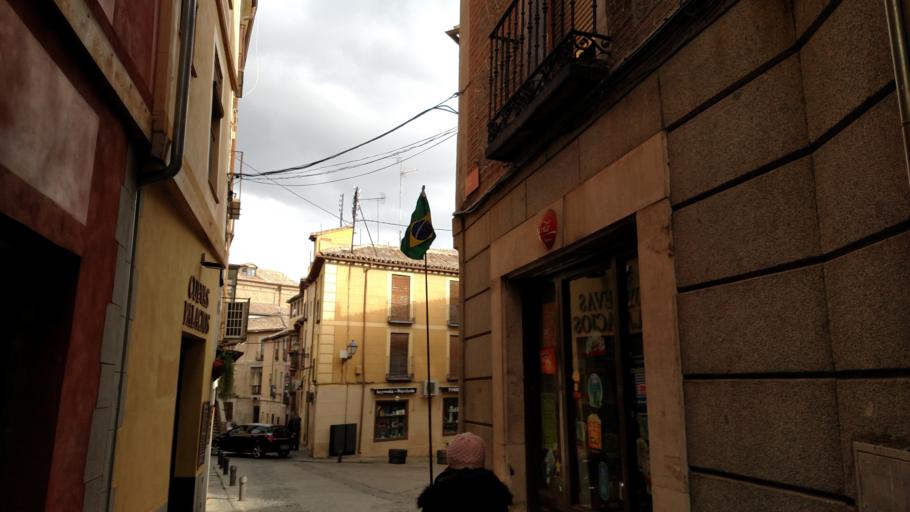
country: ES
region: Castille-La Mancha
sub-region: Province of Toledo
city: Toledo
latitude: 39.8592
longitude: -4.0257
